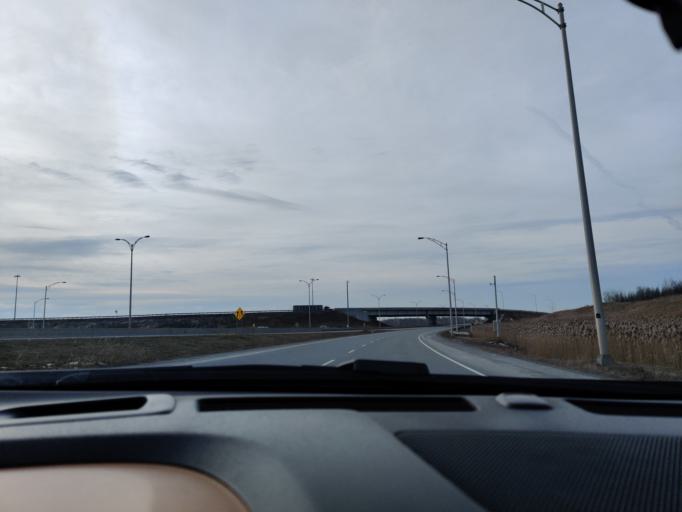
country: CA
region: Quebec
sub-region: Monteregie
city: Vaudreuil-Dorion
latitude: 45.3572
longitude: -74.0514
